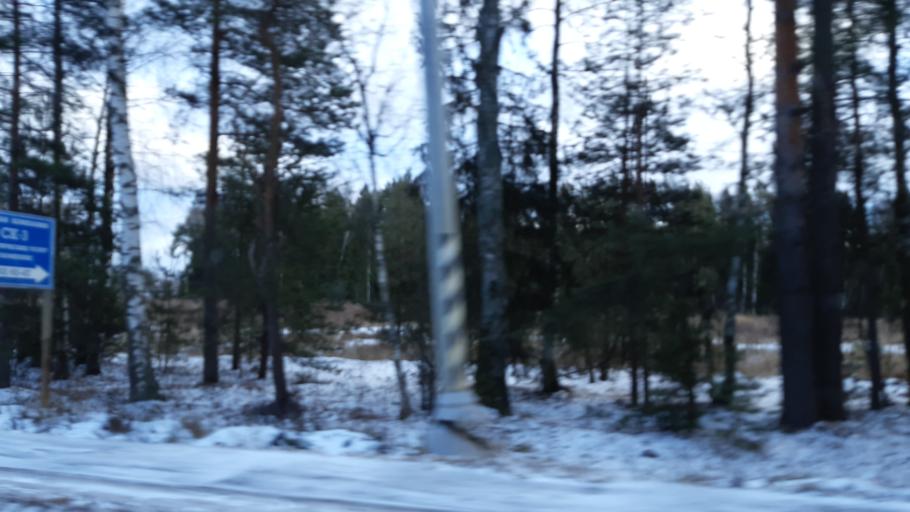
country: RU
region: Moskovskaya
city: Noginsk
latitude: 55.9435
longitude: 38.5490
